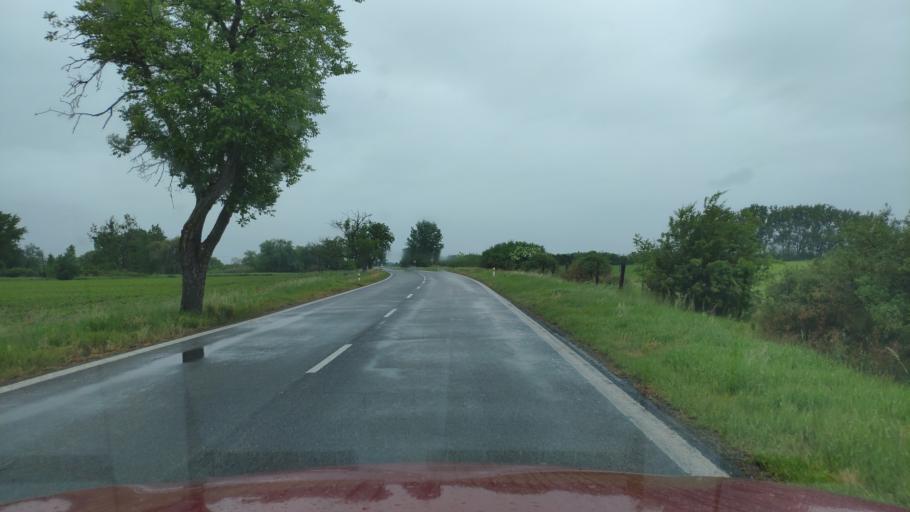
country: HU
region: Borsod-Abauj-Zemplen
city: Karcsa
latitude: 48.4093
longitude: 21.8206
